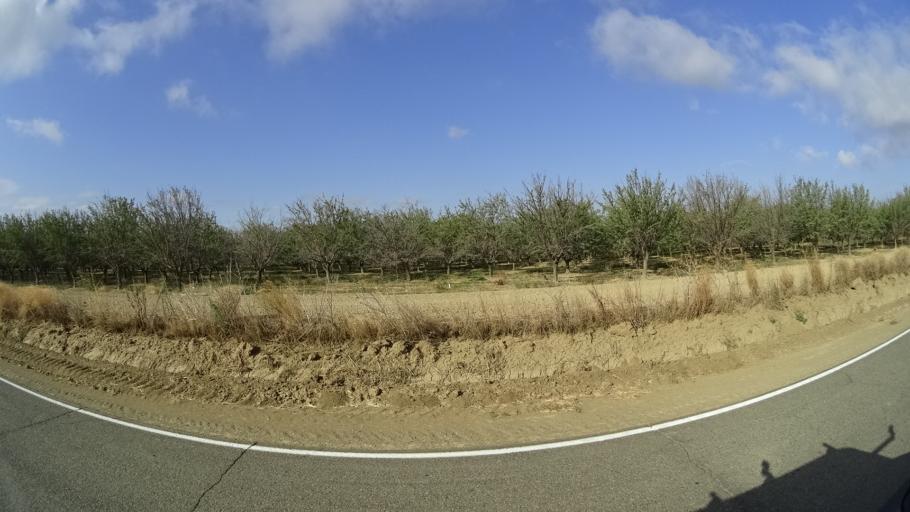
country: US
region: California
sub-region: Yolo County
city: Esparto
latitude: 38.7601
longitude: -122.0071
